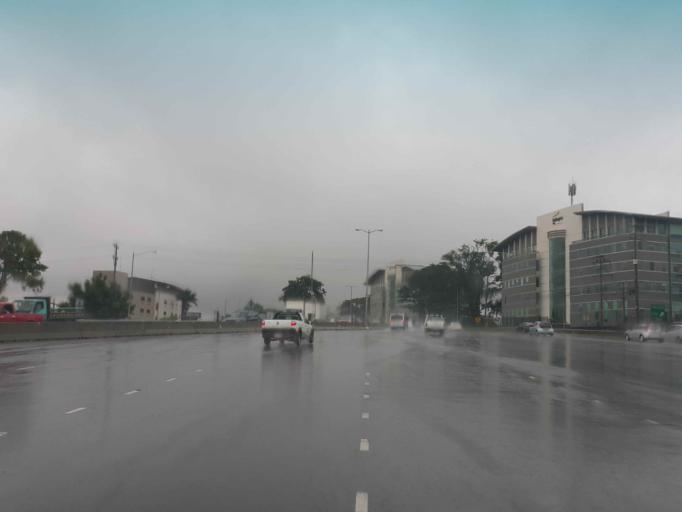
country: CR
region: San Jose
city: San Rafael
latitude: 9.9369
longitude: -84.1329
